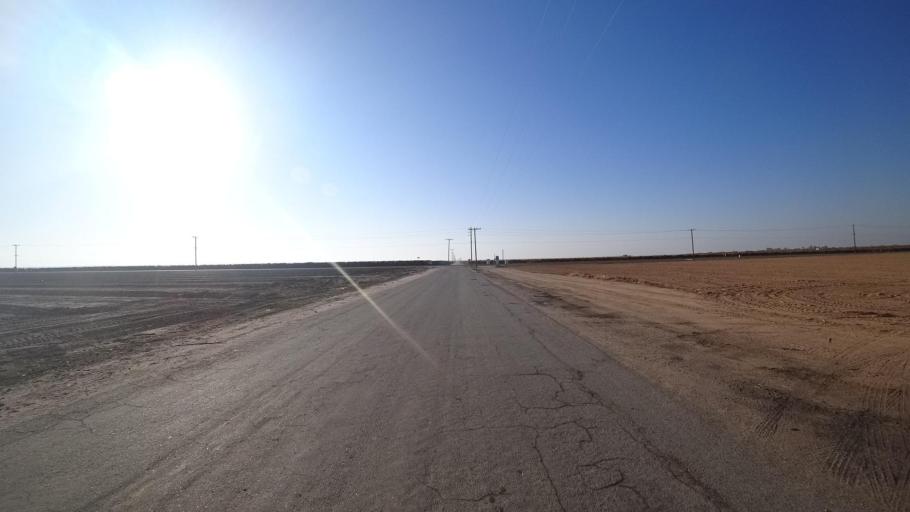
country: US
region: California
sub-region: Tulare County
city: Richgrove
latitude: 35.7624
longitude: -119.1518
